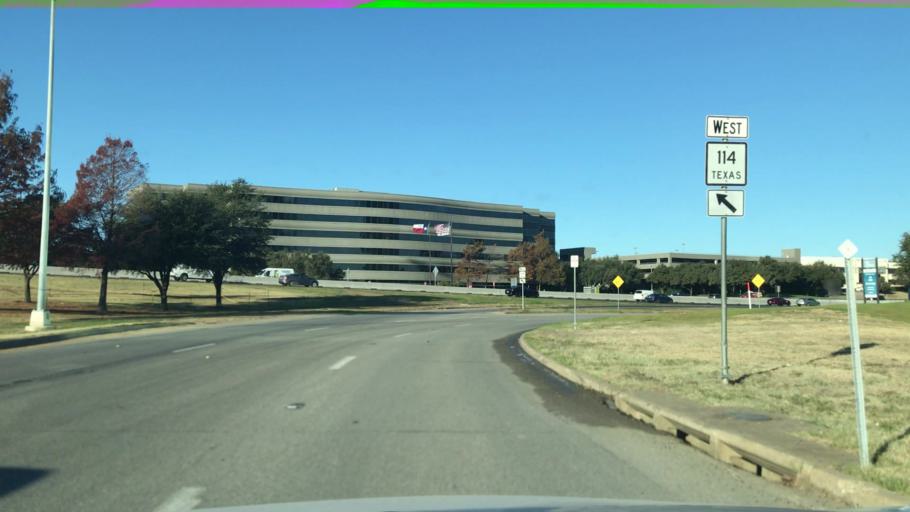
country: US
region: Texas
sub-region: Dallas County
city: Irving
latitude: 32.8698
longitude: -96.9435
